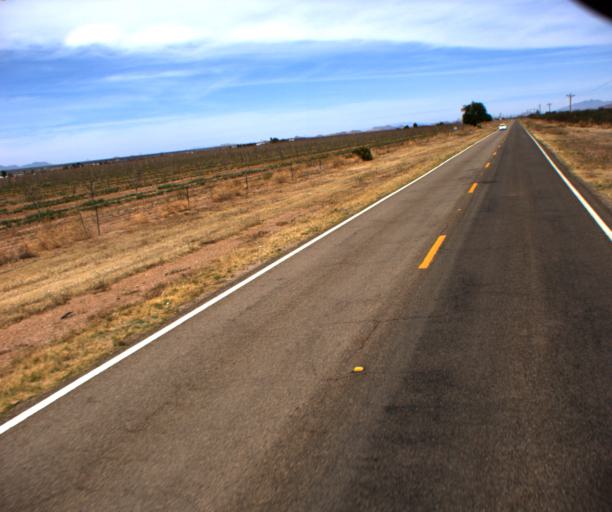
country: US
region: Arizona
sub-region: Cochise County
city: Bisbee
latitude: 31.7181
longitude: -109.6872
